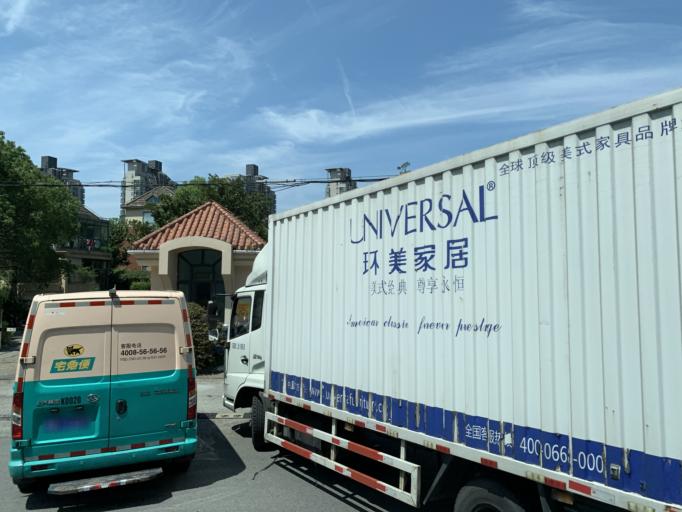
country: CN
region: Shanghai Shi
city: Huamu
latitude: 31.1788
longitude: 121.5339
